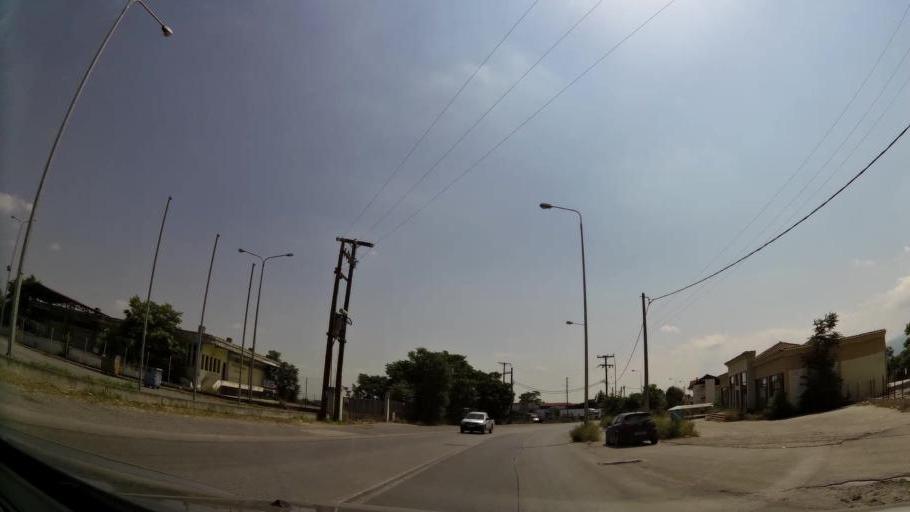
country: GR
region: Central Macedonia
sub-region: Nomos Imathias
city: Veroia
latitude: 40.5279
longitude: 22.2117
